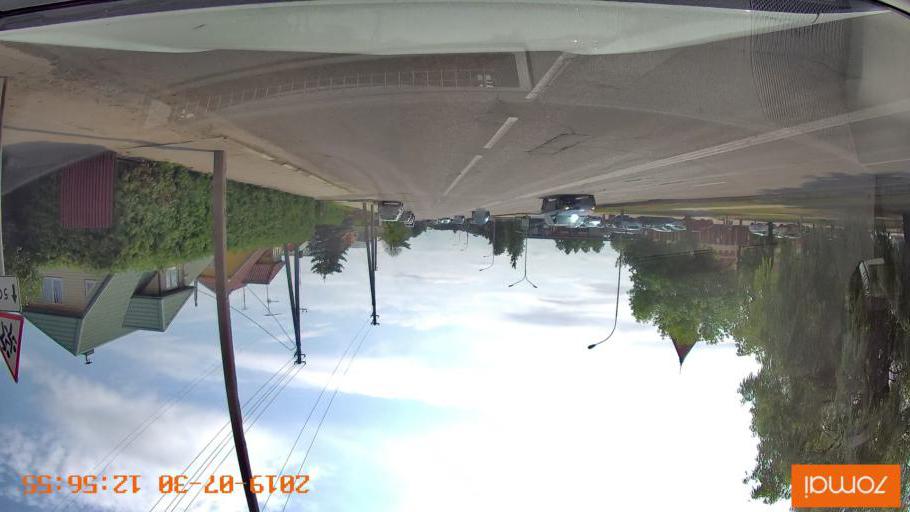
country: LT
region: Marijampoles apskritis
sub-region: Marijampole Municipality
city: Marijampole
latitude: 54.5589
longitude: 23.3640
